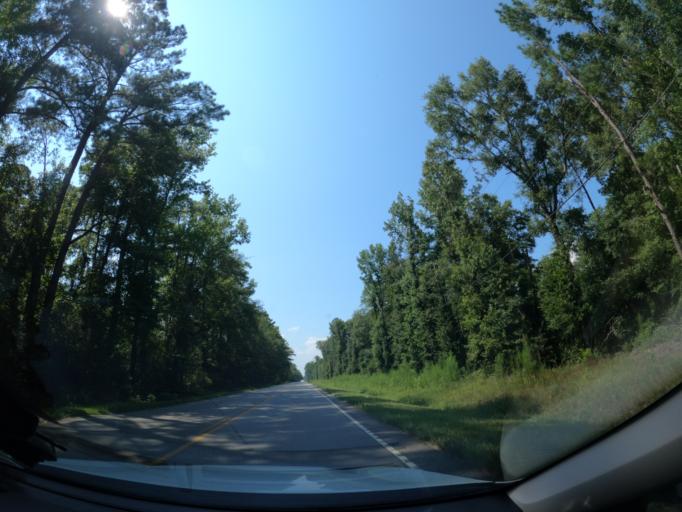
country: US
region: South Carolina
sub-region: Richland County
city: Hopkins
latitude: 33.9138
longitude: -80.9434
